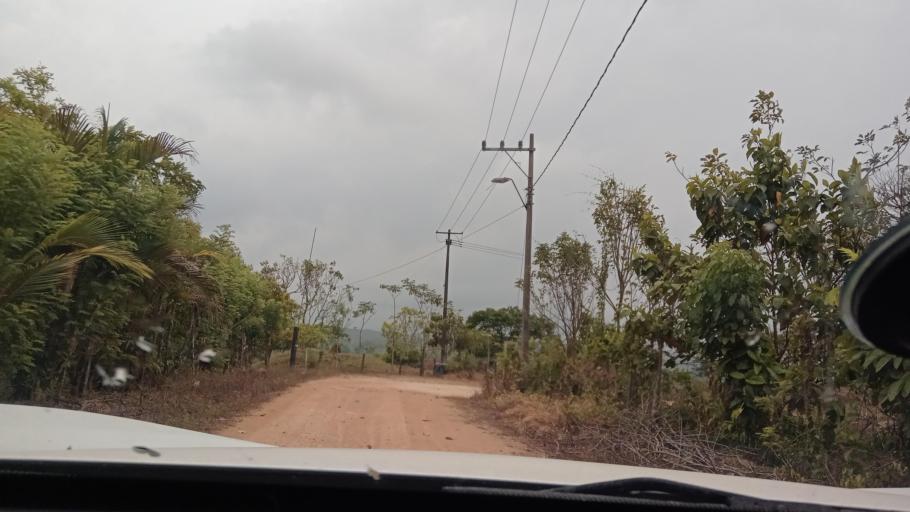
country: MX
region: Veracruz
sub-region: Uxpanapa
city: Poblado 10
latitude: 17.4473
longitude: -94.0903
